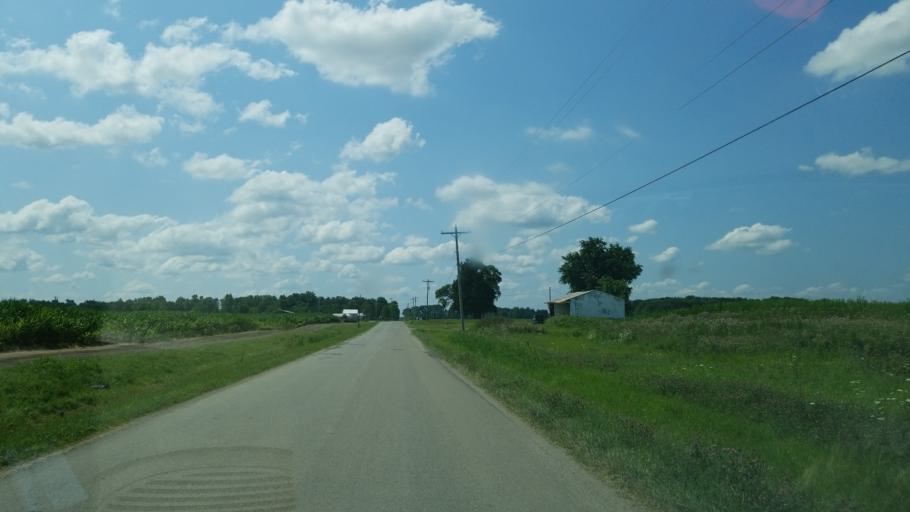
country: US
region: Ohio
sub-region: Delaware County
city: Ashley
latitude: 40.3750
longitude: -82.8539
